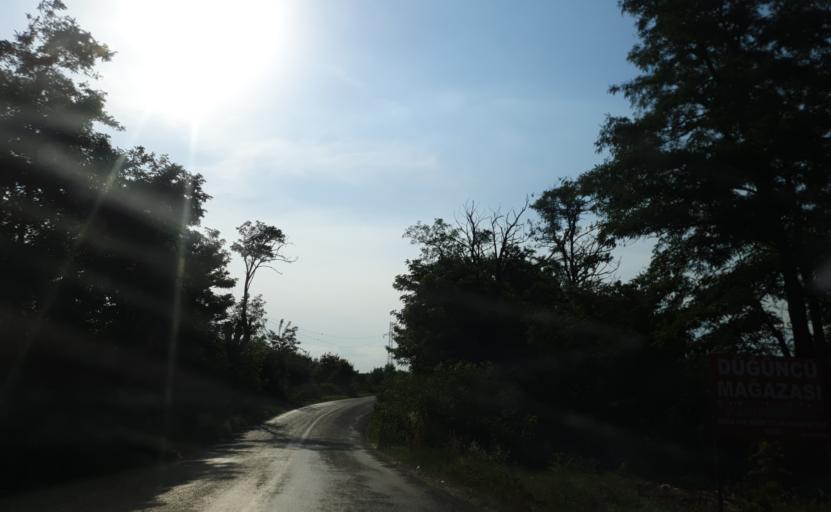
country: TR
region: Tekirdag
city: Muratli
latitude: 41.1939
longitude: 27.4755
